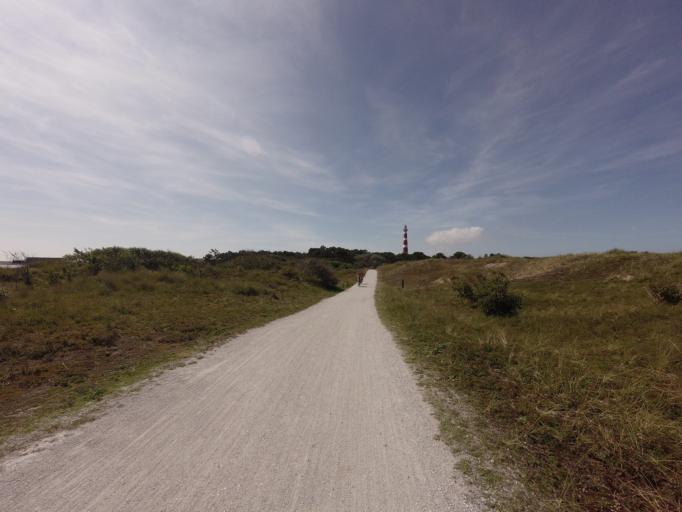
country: NL
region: Friesland
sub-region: Gemeente Ameland
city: Hollum
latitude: 53.4504
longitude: 5.6317
